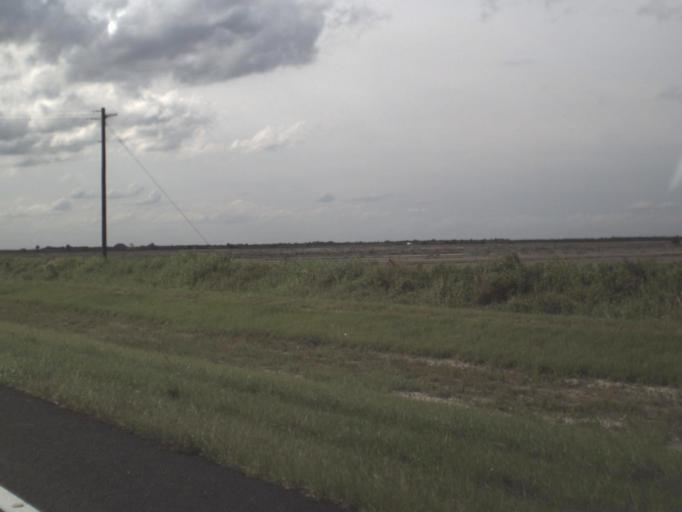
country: US
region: Florida
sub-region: Glades County
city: Moore Haven
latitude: 26.7533
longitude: -81.1043
